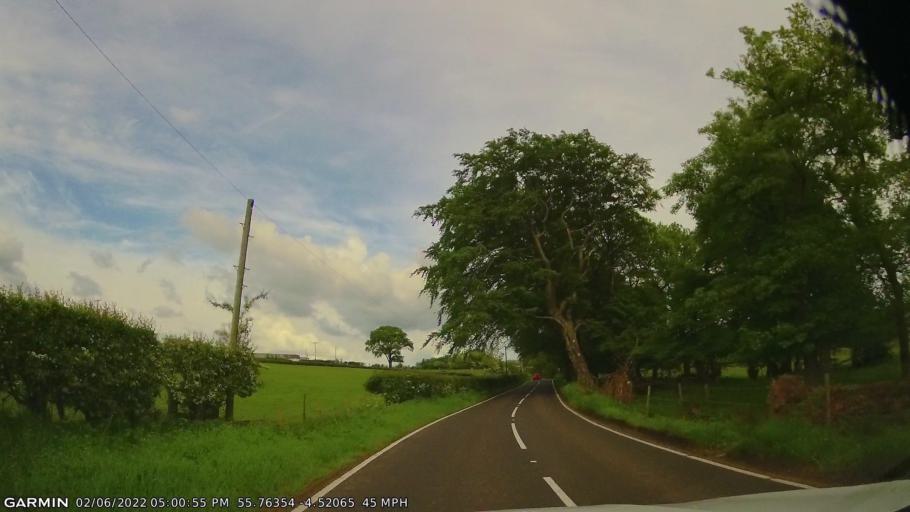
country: GB
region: Scotland
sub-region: Renfrewshire
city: Howwood
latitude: 55.7635
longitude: -4.5207
